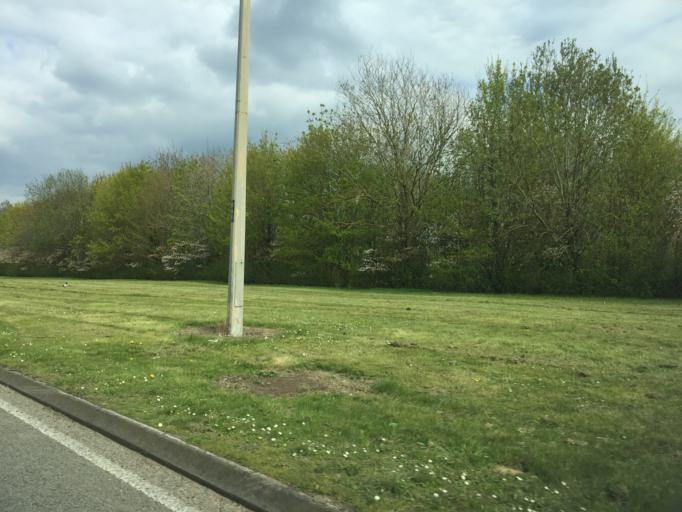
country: GB
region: England
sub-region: Milton Keynes
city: Shenley Church End
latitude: 52.0129
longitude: -0.7762
